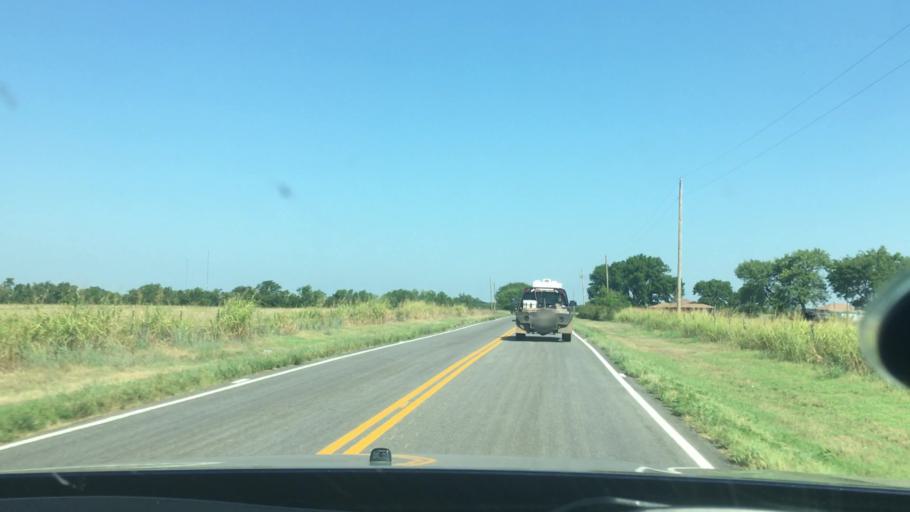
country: US
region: Oklahoma
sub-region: Johnston County
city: Tishomingo
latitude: 34.1837
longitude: -96.5141
